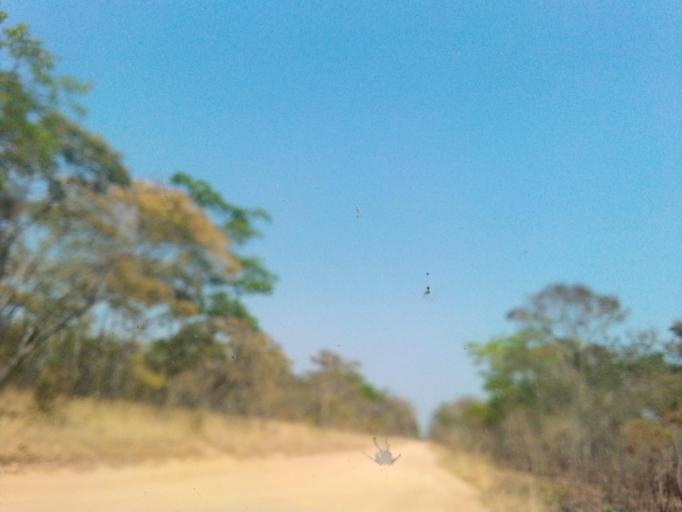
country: ZM
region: Northern
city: Mpika
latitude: -12.2419
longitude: 30.8504
